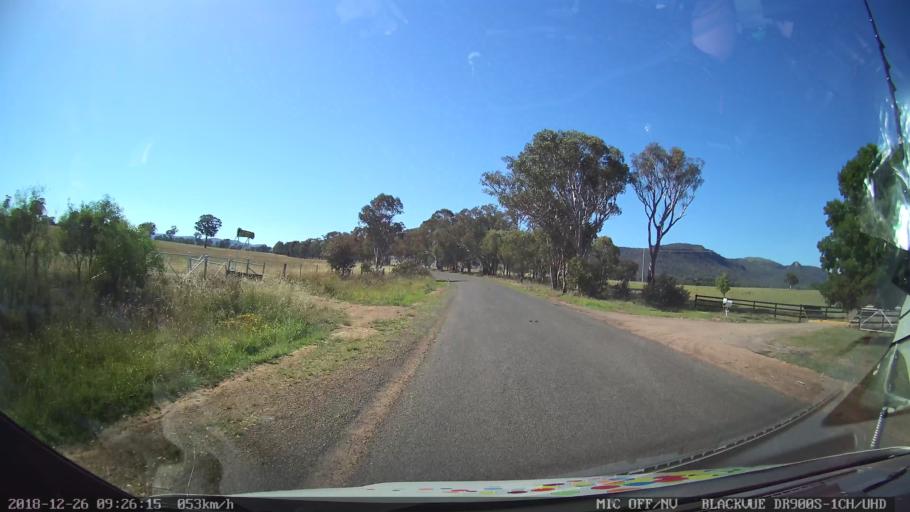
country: AU
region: New South Wales
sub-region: Mid-Western Regional
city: Kandos
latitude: -32.8272
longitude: 150.0071
